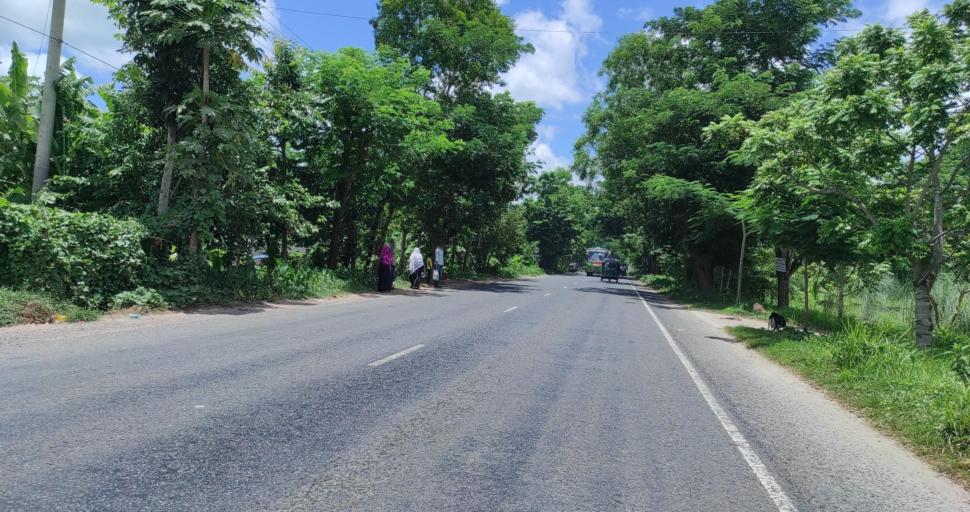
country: BD
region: Barisal
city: Gaurnadi
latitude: 22.8364
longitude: 90.2531
